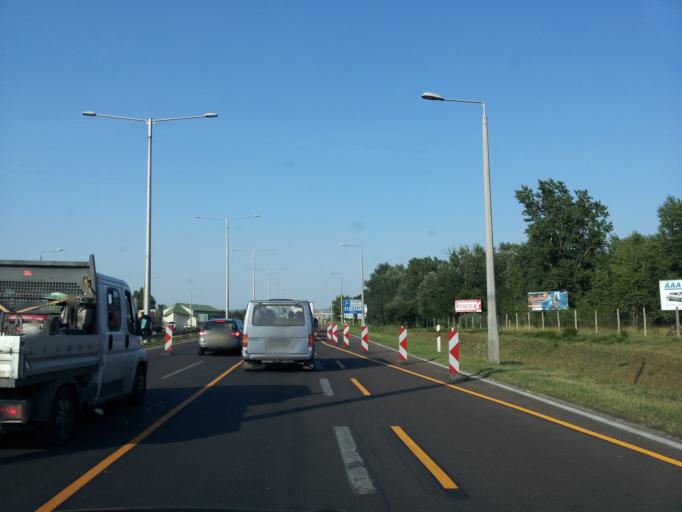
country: HU
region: Budapest
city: Budapest XV. keruelet
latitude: 47.5588
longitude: 19.1344
